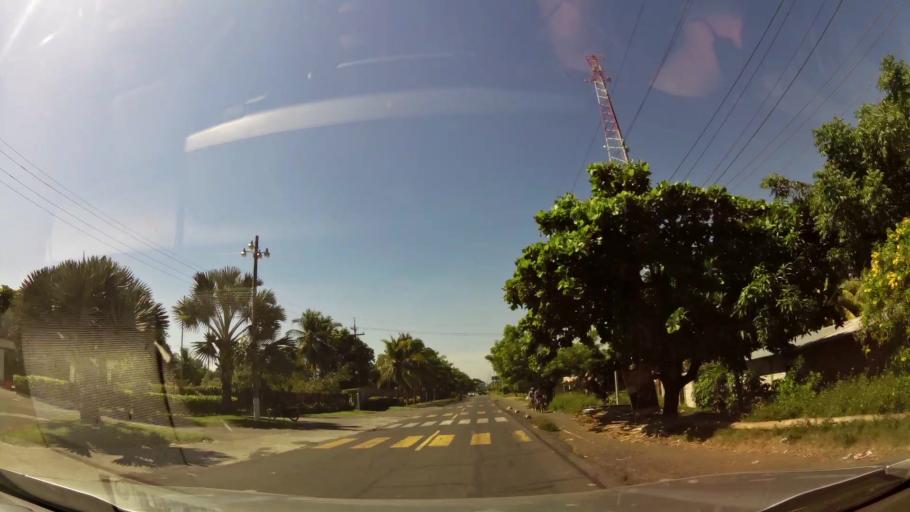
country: GT
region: Escuintla
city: Iztapa
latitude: 13.9337
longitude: -90.7625
